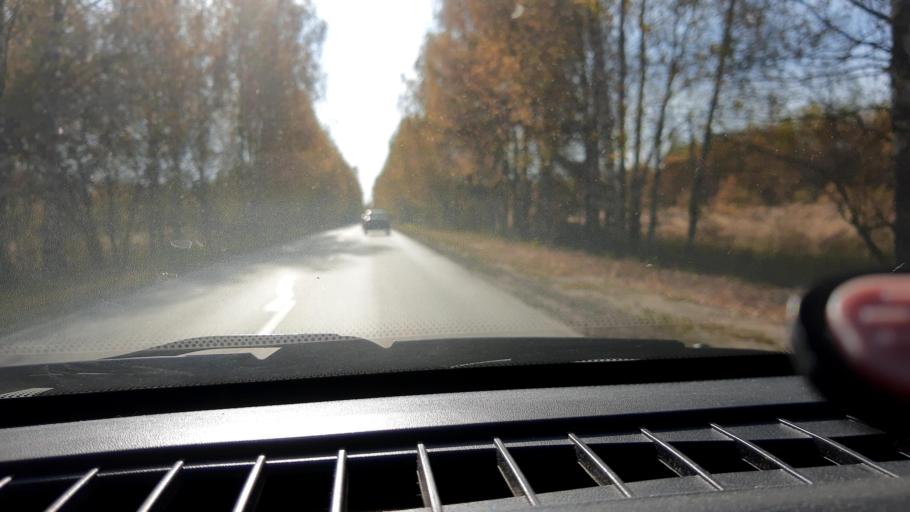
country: RU
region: Nizjnij Novgorod
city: Neklyudovo
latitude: 56.5176
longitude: 43.8375
